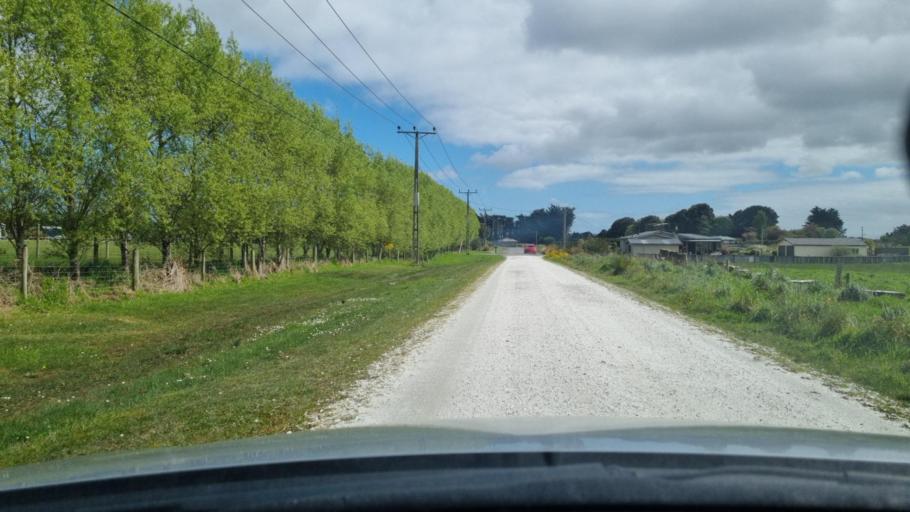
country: NZ
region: Southland
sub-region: Invercargill City
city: Invercargill
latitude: -46.4432
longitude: 168.3855
